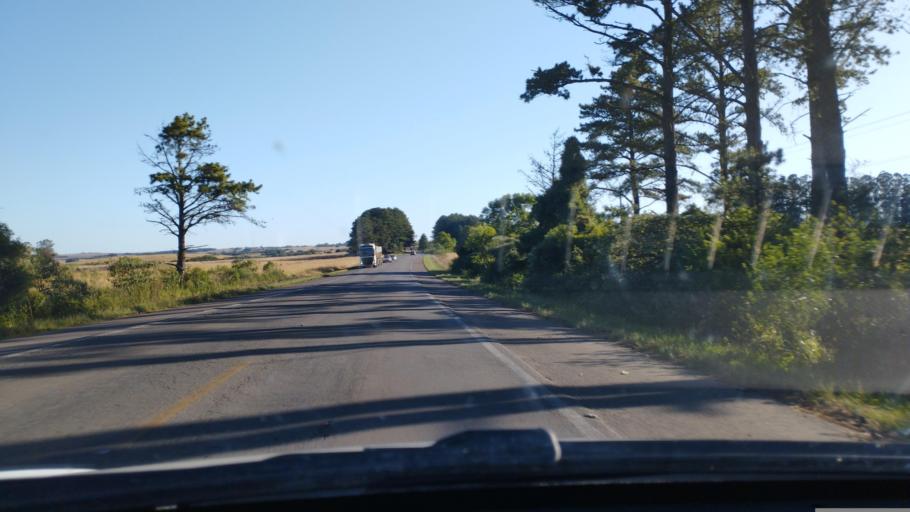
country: BR
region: Rio Grande do Sul
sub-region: Julio De Castilhos
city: Julio de Castilhos
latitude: -29.4316
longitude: -53.6755
